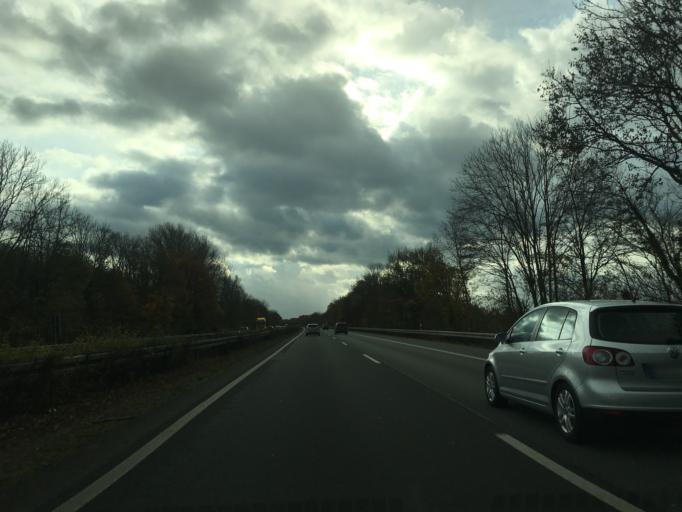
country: DE
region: North Rhine-Westphalia
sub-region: Regierungsbezirk Munster
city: Ascheberg
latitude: 51.7684
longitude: 7.6406
